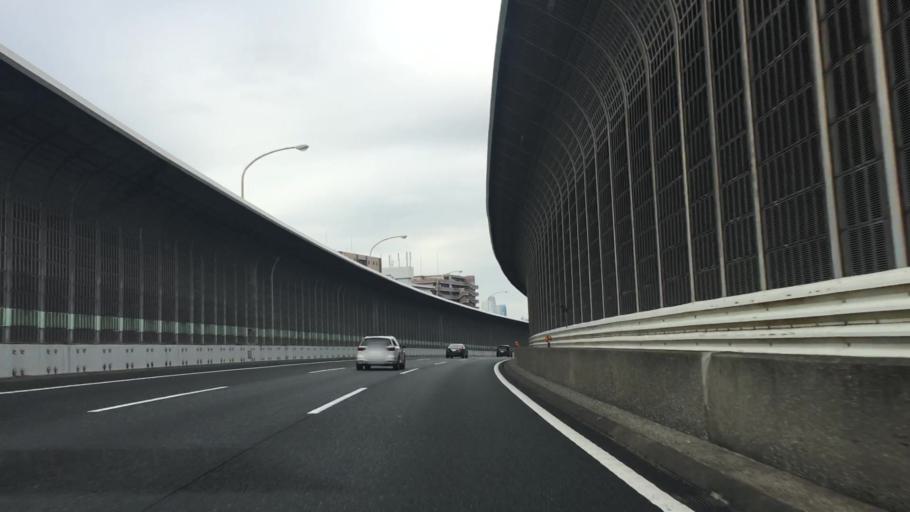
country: JP
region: Chiba
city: Chiba
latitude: 35.6427
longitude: 140.0709
